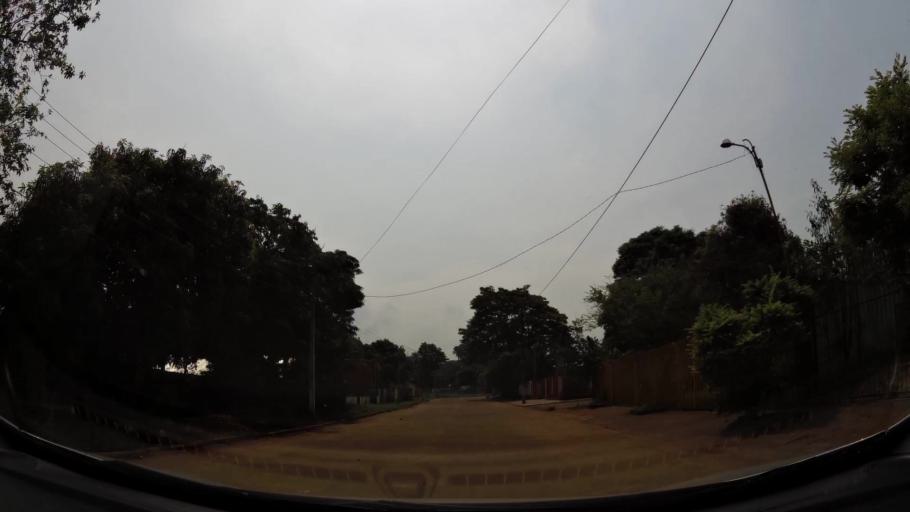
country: PY
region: Alto Parana
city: Presidente Franco
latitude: -25.5644
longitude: -54.6171
